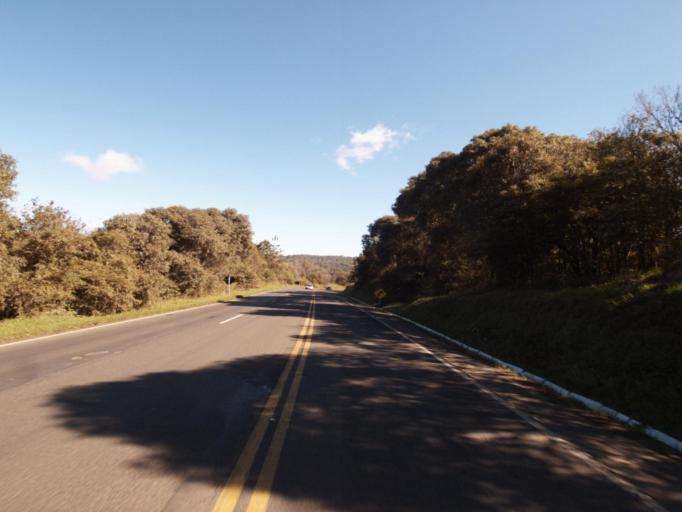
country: BR
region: Santa Catarina
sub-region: Joacaba
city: Joacaba
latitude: -27.1716
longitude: -51.5566
